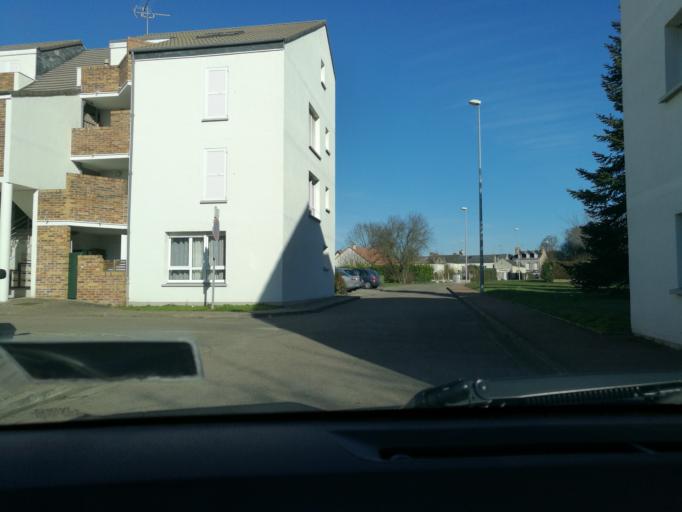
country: FR
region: Centre
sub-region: Departement du Loiret
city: Saint-Jean-de-la-Ruelle
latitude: 47.9094
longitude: 1.8788
